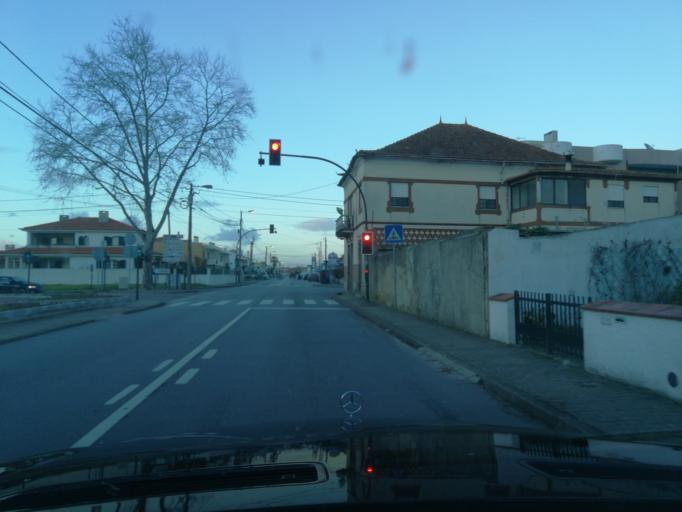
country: PT
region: Aveiro
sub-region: Estarreja
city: Estarreja
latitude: 40.7627
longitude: -8.5712
